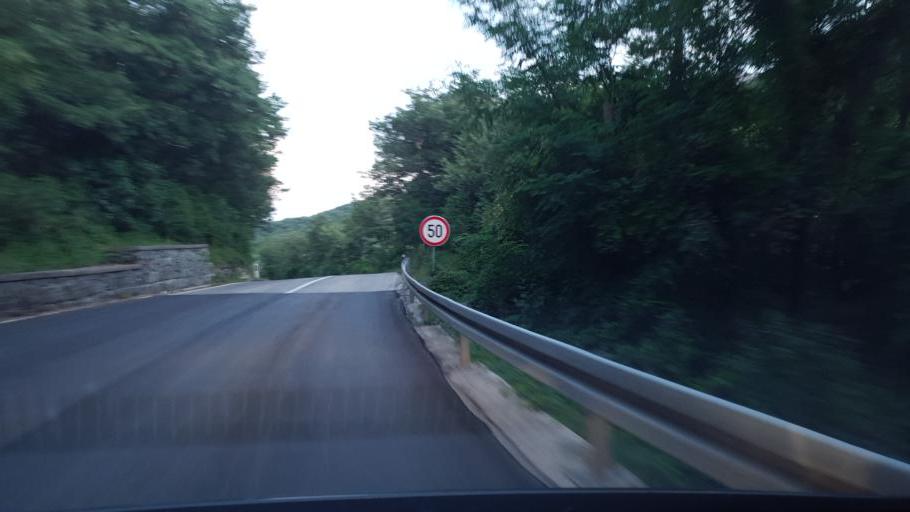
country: HR
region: Primorsko-Goranska
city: Punat
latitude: 45.0195
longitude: 14.6898
